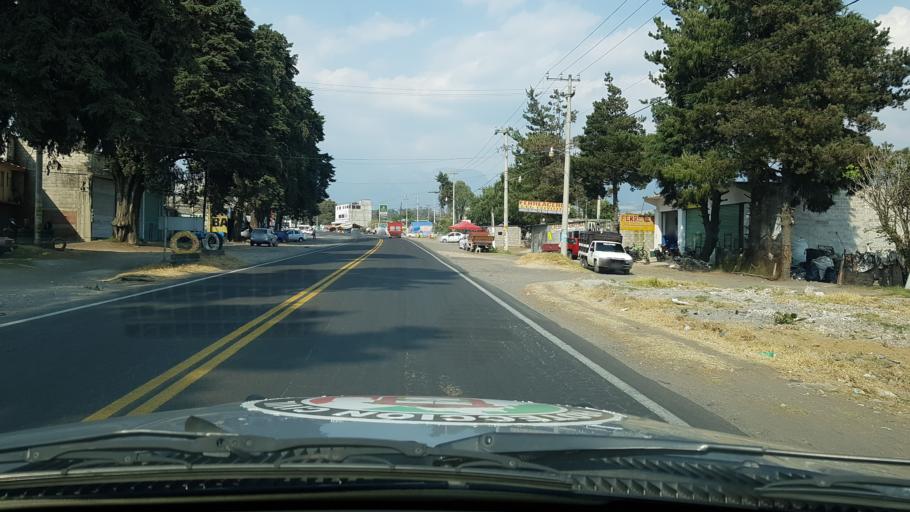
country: MX
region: Mexico
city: Ozumba de Alzate
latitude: 19.0456
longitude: -98.7958
